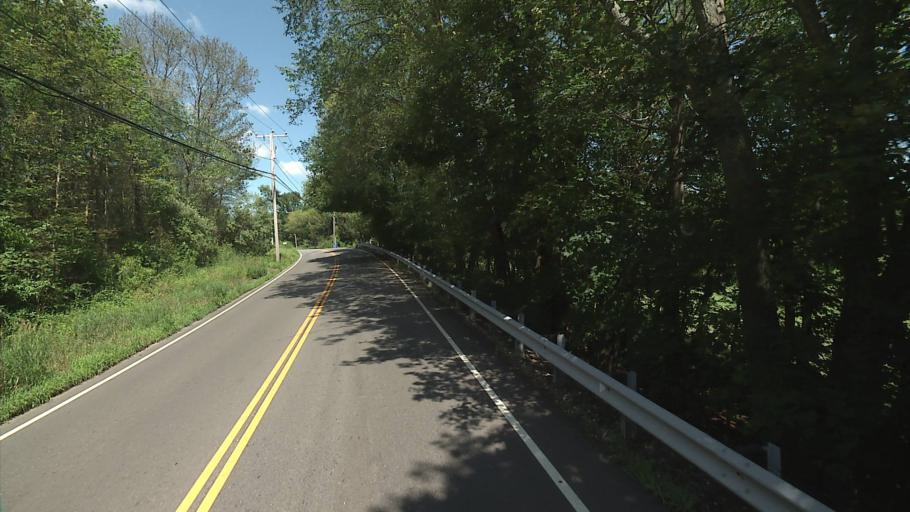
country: US
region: Connecticut
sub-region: Windham County
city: Plainfield Village
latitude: 41.6853
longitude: -71.9323
